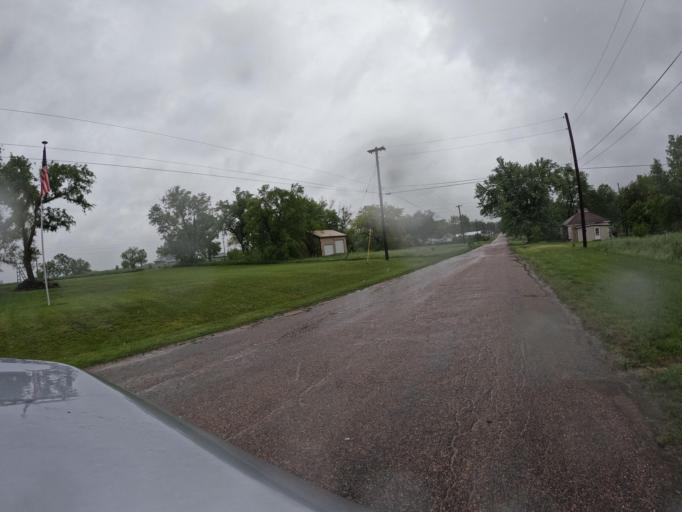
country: US
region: Nebraska
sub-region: Gage County
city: Wymore
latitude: 40.1262
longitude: -96.6559
